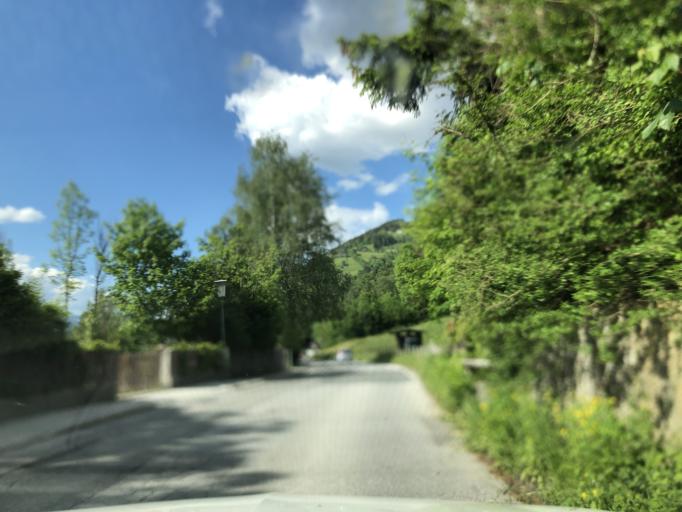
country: AT
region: Salzburg
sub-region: Politischer Bezirk Zell am See
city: Bruck an der Grossglocknerstrasse
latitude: 47.3065
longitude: 12.8156
